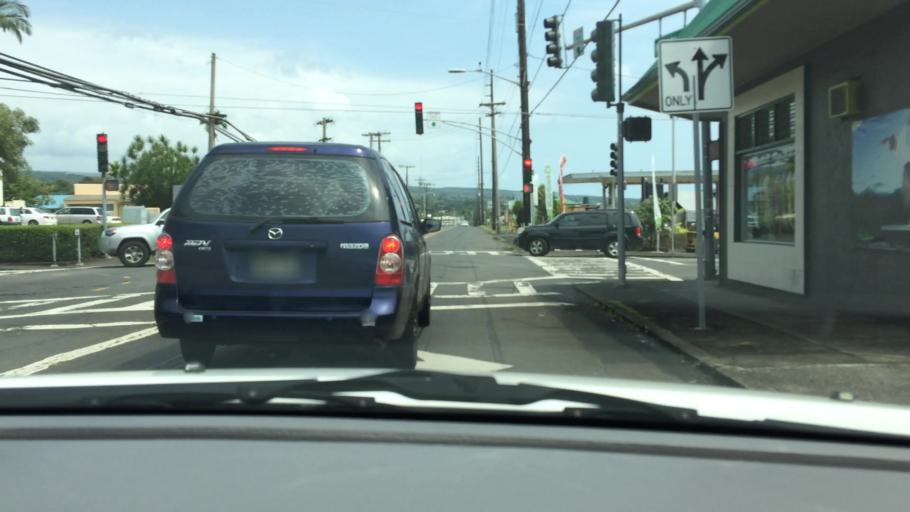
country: US
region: Hawaii
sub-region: Hawaii County
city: Hilo
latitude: 19.7160
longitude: -155.0831
